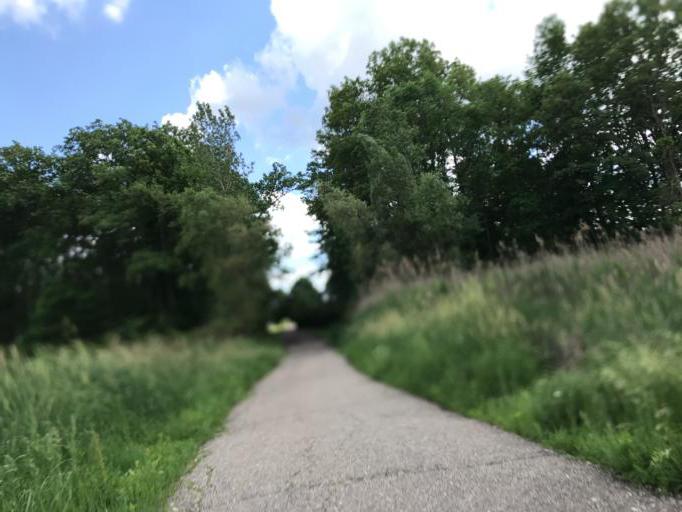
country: US
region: Michigan
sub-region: Oakland County
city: South Lyon
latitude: 42.4537
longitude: -83.6608
